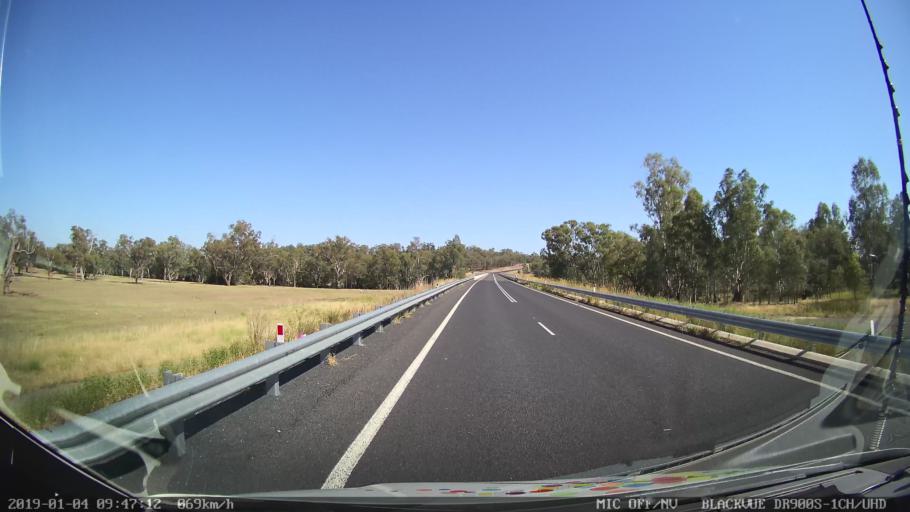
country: AU
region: New South Wales
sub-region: Cabonne
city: Canowindra
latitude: -33.6087
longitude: 148.4331
